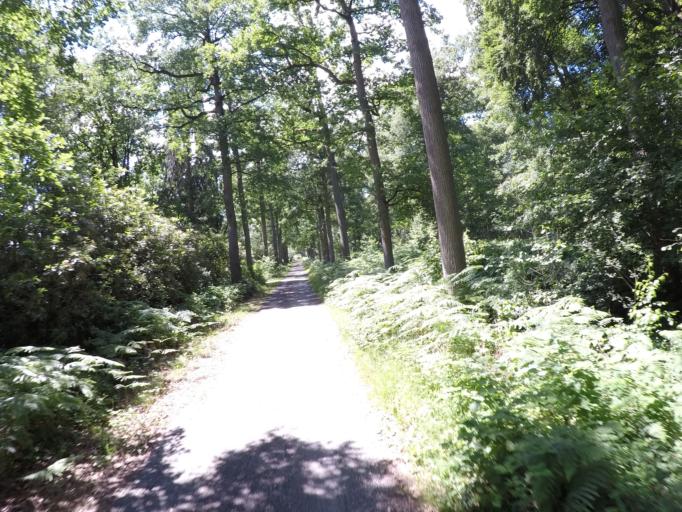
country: BE
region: Flanders
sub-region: Provincie Antwerpen
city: Vosselaar
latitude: 51.2873
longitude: 4.8853
